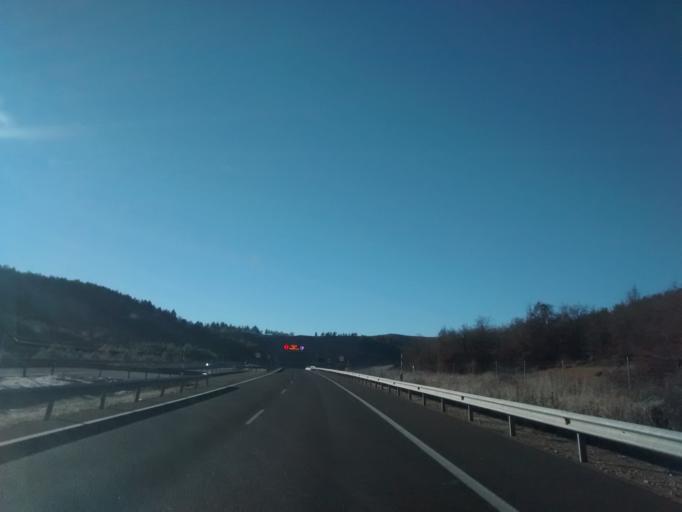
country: ES
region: Castille and Leon
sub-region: Provincia de Palencia
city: Alar del Rey
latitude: 42.6920
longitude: -4.2988
